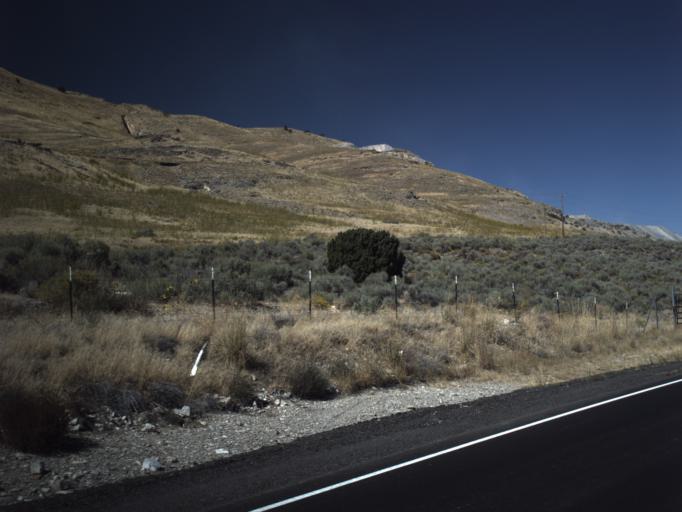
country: US
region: Utah
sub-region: Utah County
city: Saratoga Springs
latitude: 40.2441
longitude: -111.8664
